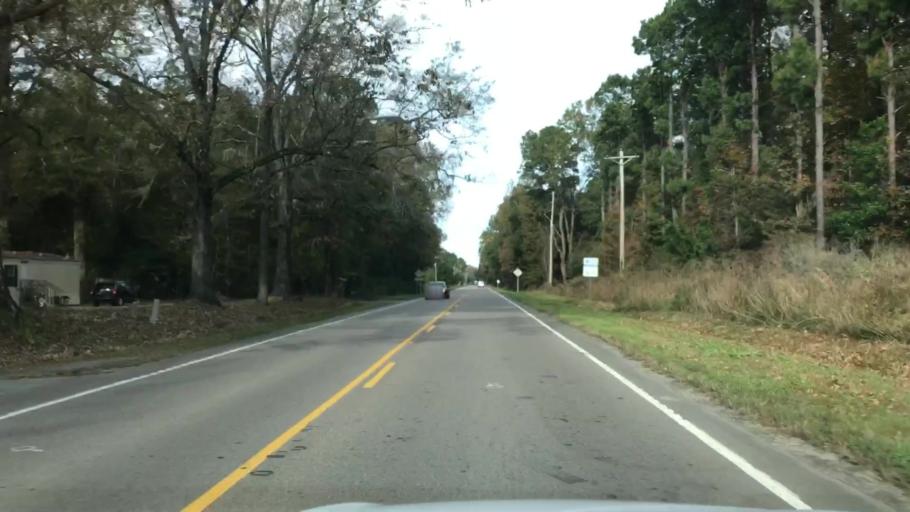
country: US
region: South Carolina
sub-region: Colleton County
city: Walterboro
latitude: 32.8255
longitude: -80.5598
